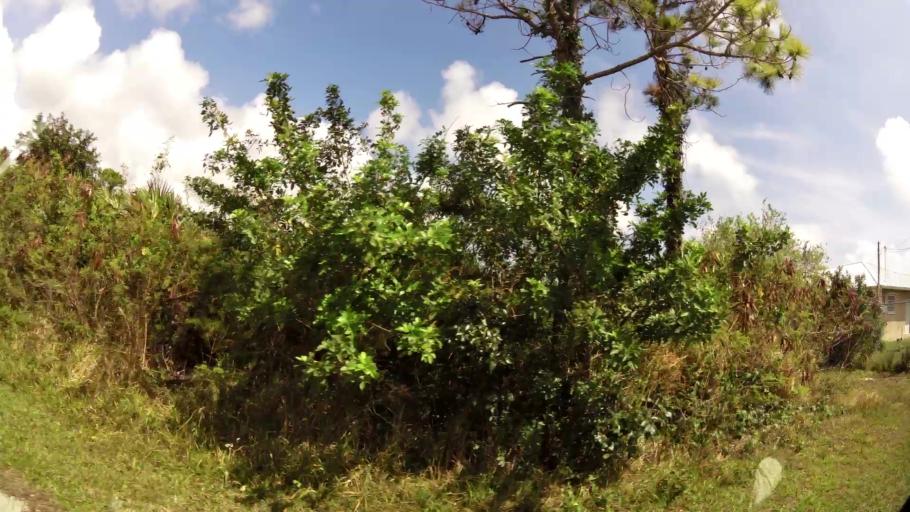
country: BS
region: Freeport
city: Freeport
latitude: 26.5133
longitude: -78.7269
